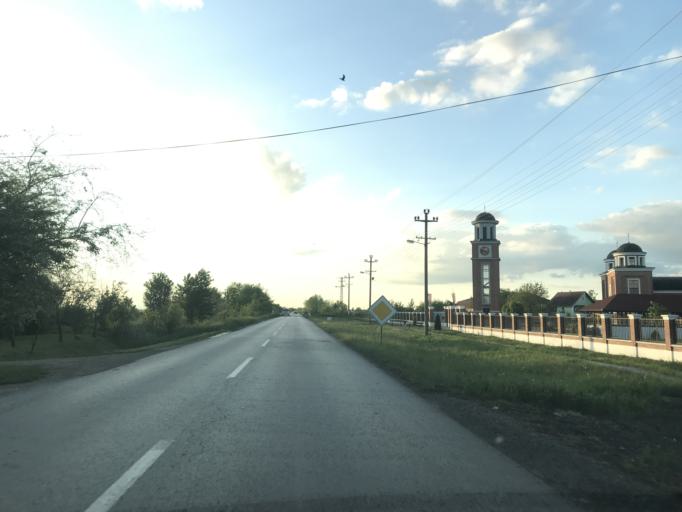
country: RS
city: Banatski Dvor
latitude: 45.5227
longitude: 20.5123
